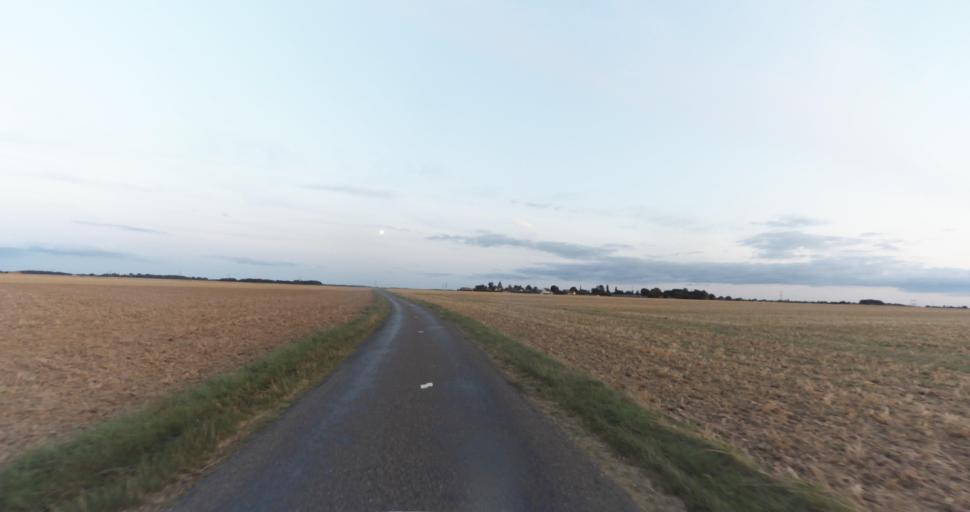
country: FR
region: Haute-Normandie
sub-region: Departement de l'Eure
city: La Madeleine-de-Nonancourt
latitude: 48.8754
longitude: 1.2447
